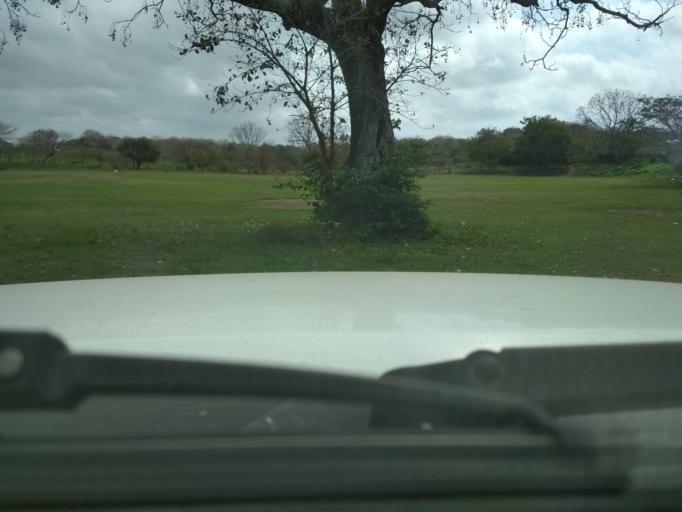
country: MX
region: Veracruz
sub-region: Veracruz
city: Delfino Victoria (Santa Fe)
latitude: 19.2504
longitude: -96.2623
